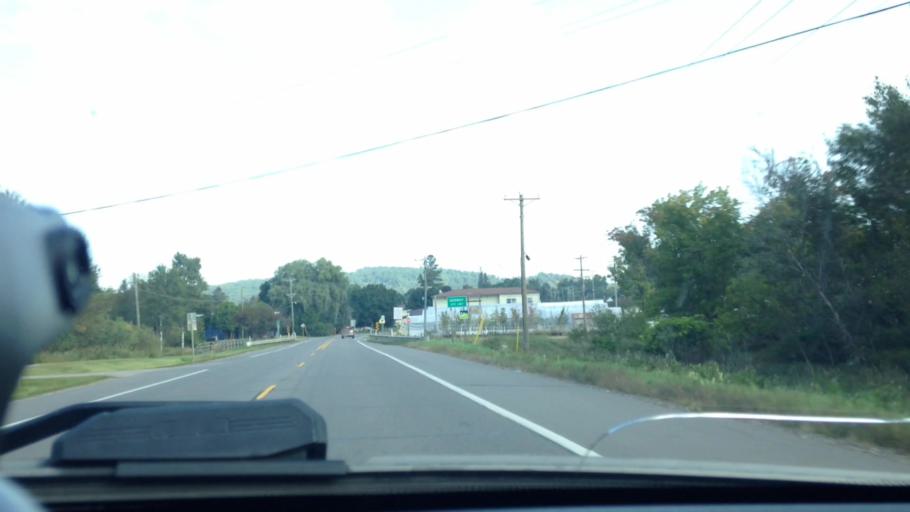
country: US
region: Michigan
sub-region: Dickinson County
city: Norway
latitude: 45.7793
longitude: -87.9093
